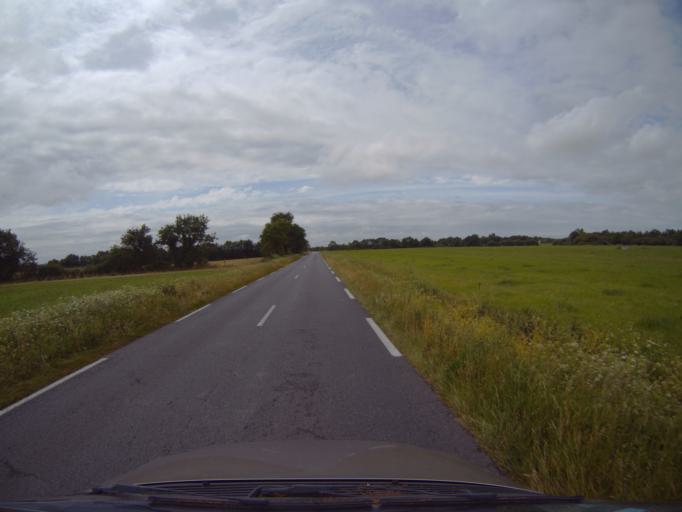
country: FR
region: Pays de la Loire
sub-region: Departement de la Loire-Atlantique
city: Montbert
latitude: 47.0598
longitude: -1.4544
